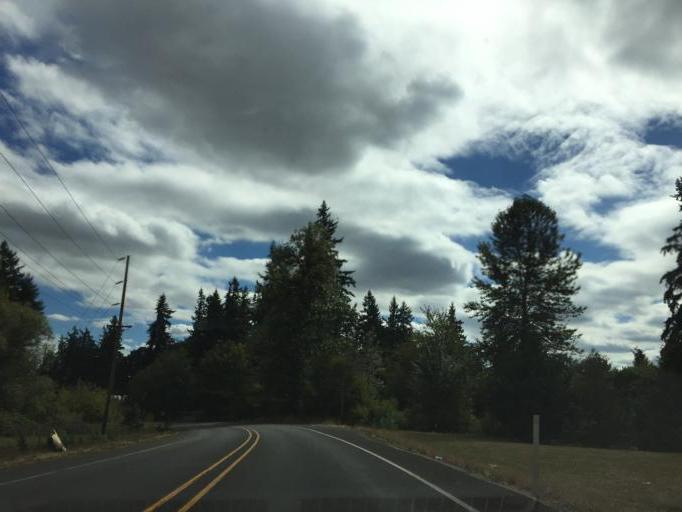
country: US
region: Oregon
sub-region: Marion County
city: Woodburn
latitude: 45.1312
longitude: -122.8319
